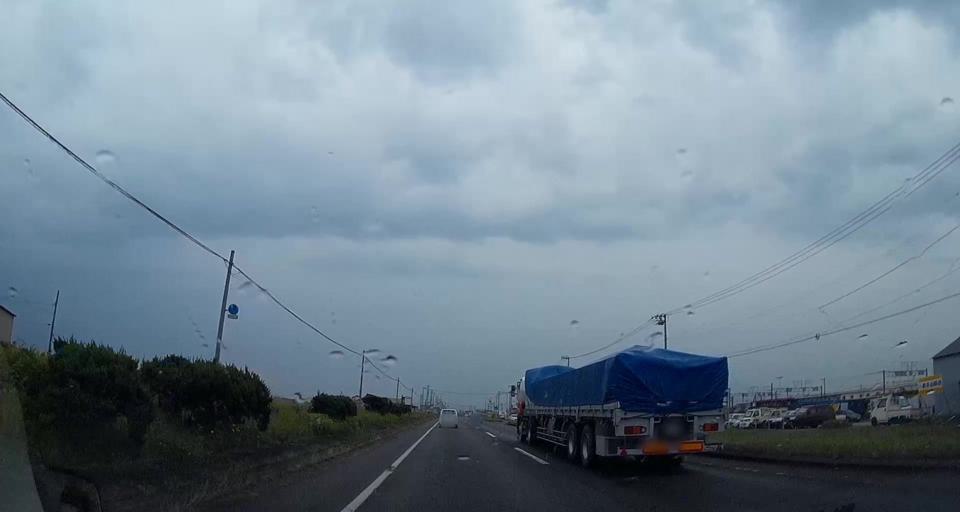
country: JP
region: Hokkaido
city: Tomakomai
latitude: 42.6012
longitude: 141.4863
